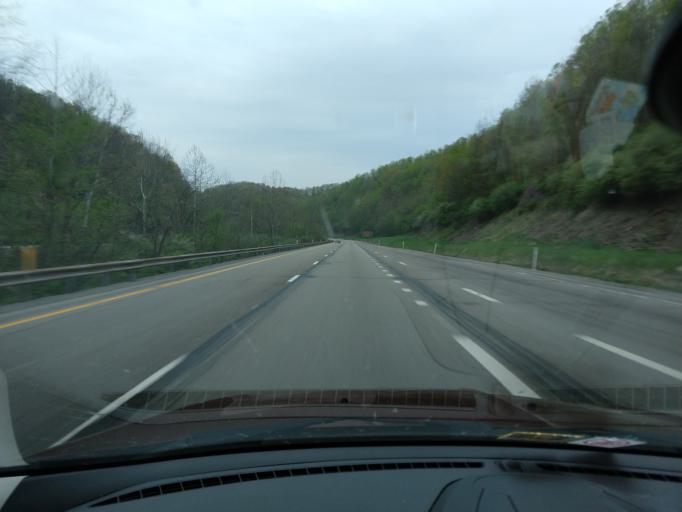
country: US
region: West Virginia
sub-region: Lewis County
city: Weston
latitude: 39.0132
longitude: -80.4655
